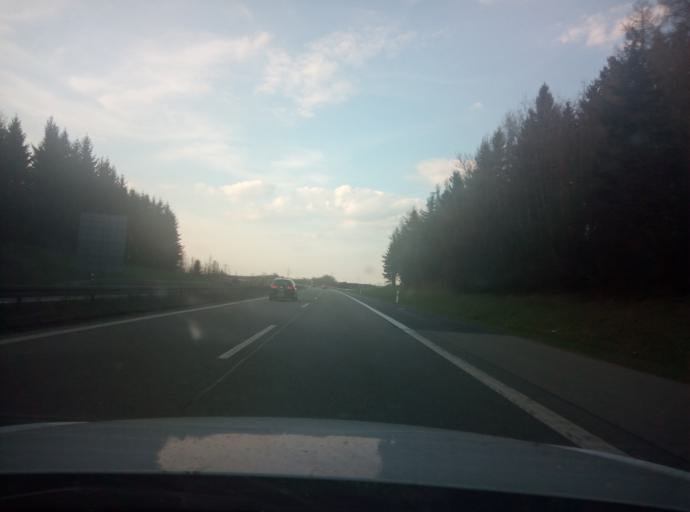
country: DE
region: Baden-Wuerttemberg
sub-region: Freiburg Region
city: Tuningen
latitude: 48.0368
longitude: 8.6217
